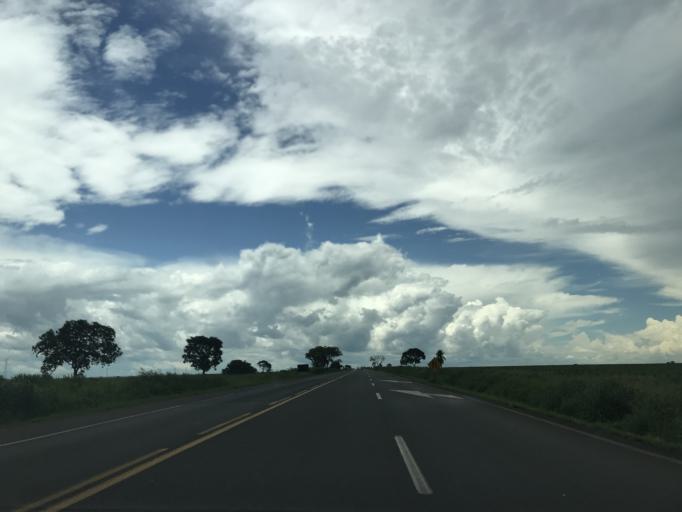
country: BR
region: Minas Gerais
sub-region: Monte Alegre De Minas
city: Monte Alegre de Minas
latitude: -19.0179
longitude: -49.0148
